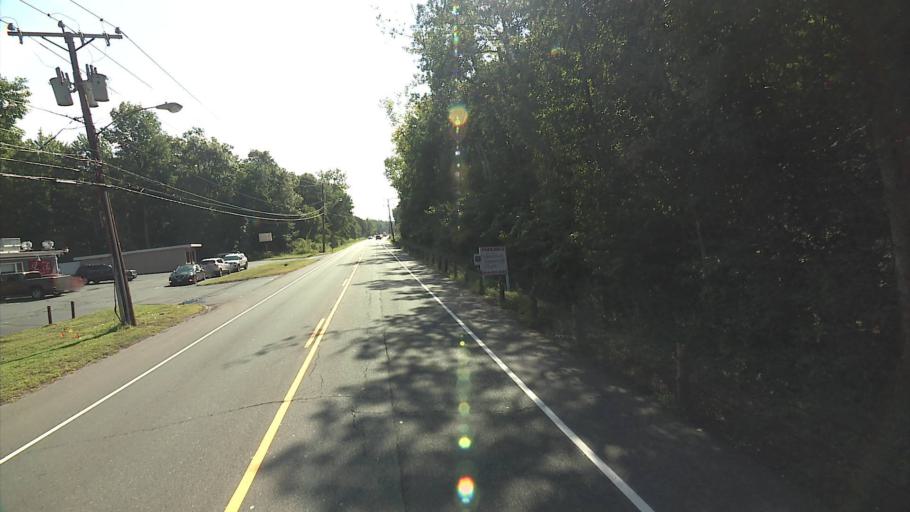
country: US
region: Connecticut
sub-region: Hartford County
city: Hazardville
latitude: 41.9886
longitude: -72.5645
